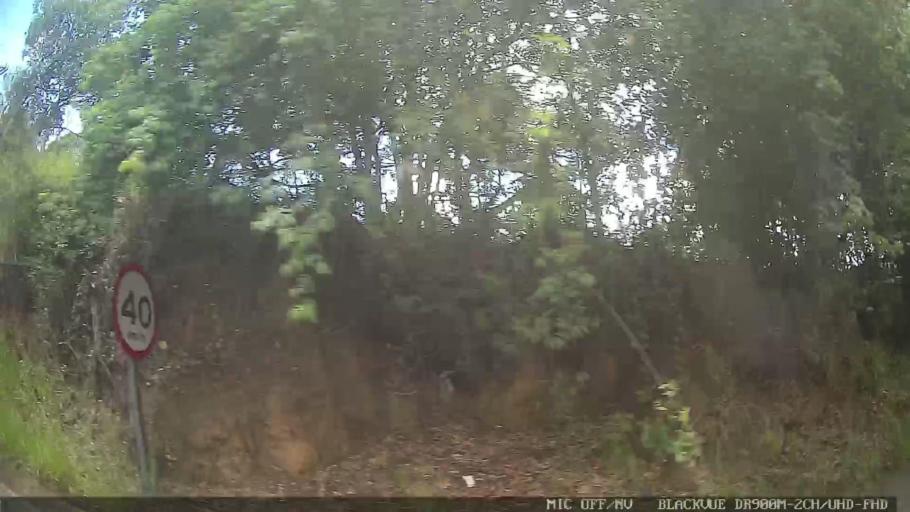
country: BR
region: Sao Paulo
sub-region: Braganca Paulista
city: Braganca Paulista
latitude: -22.9852
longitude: -46.4775
